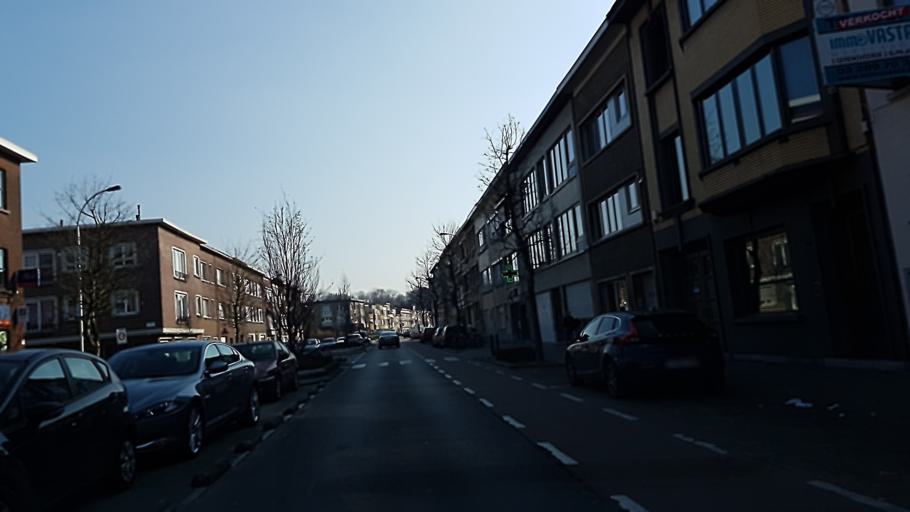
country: BE
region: Flanders
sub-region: Provincie Antwerpen
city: Borsbeek
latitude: 51.2072
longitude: 4.4494
